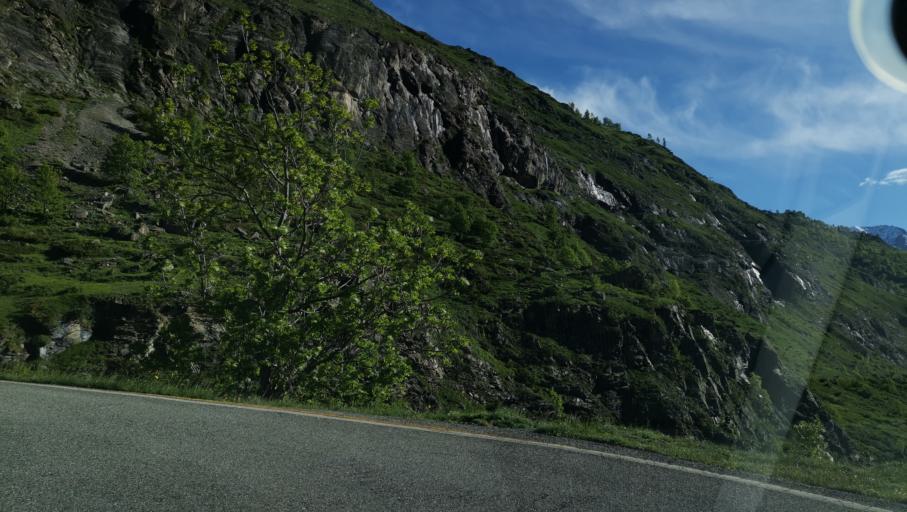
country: IT
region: Piedmont
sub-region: Provincia di Torino
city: Usseglio
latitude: 45.2095
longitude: 7.1653
